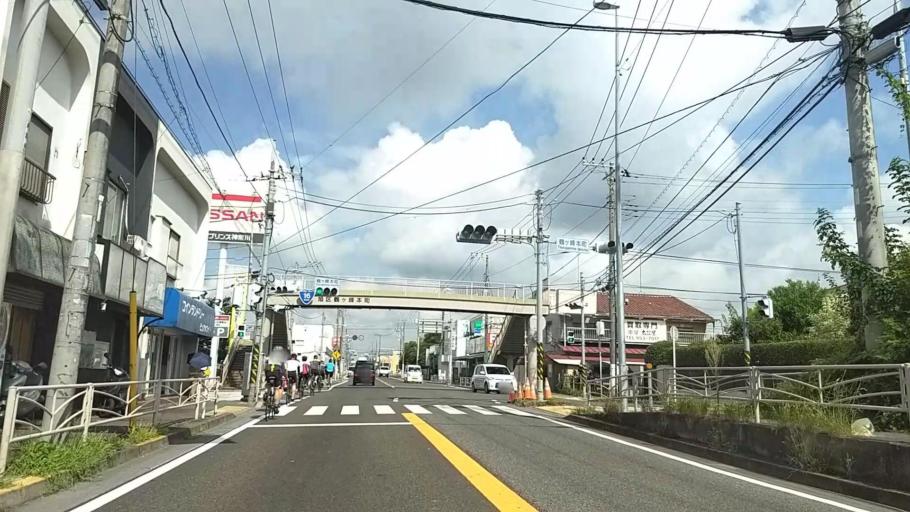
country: JP
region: Kanagawa
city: Minami-rinkan
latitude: 35.4789
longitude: 139.5380
